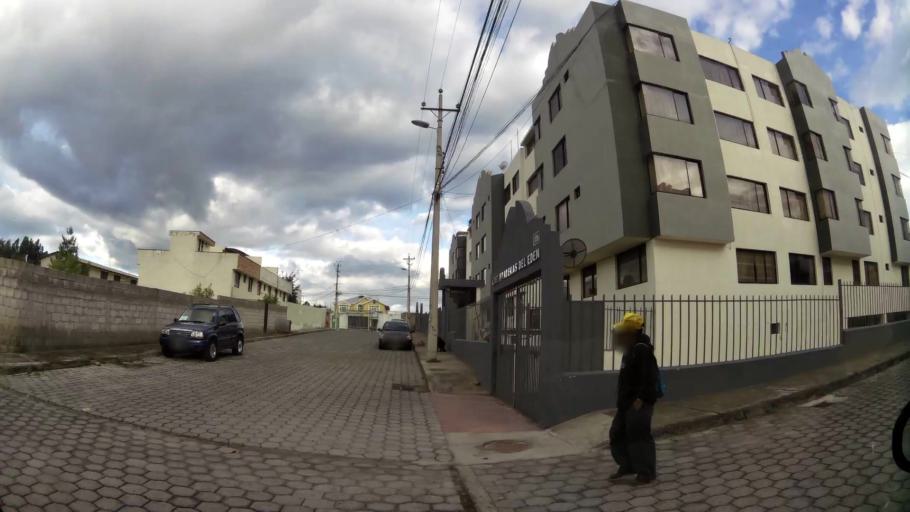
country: EC
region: Pichincha
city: Quito
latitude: -0.1305
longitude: -78.4626
